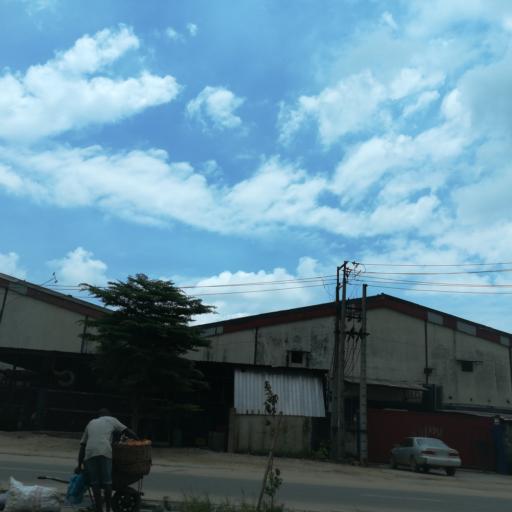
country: NG
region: Lagos
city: Oshodi
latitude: 6.5583
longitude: 3.3591
